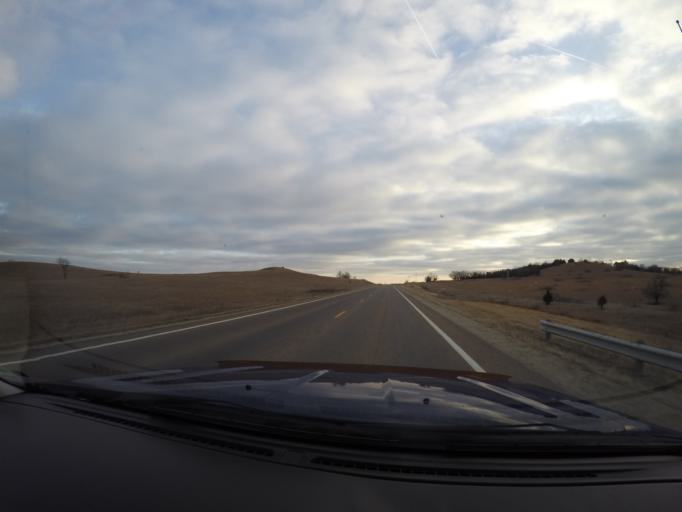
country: US
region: Kansas
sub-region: Morris County
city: Council Grove
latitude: 38.7173
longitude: -96.4976
